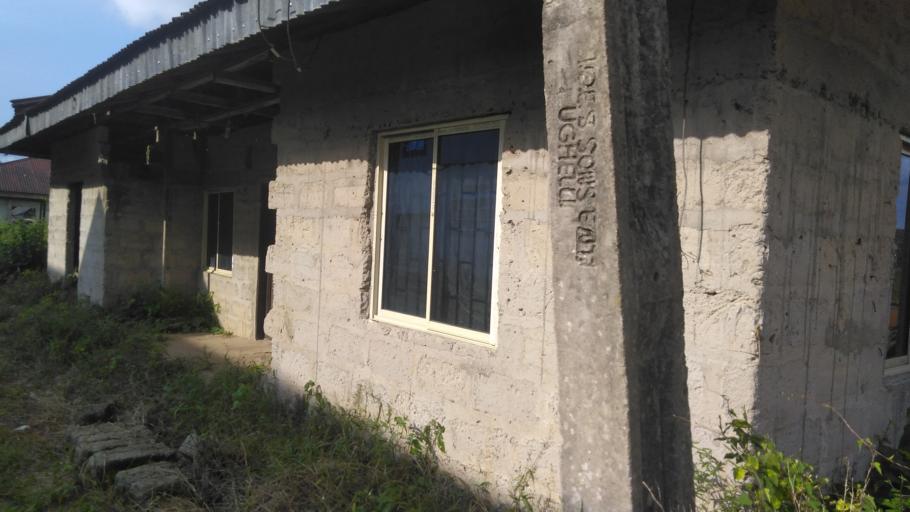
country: NG
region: Edo
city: Siluko
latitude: 6.1432
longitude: 5.1999
